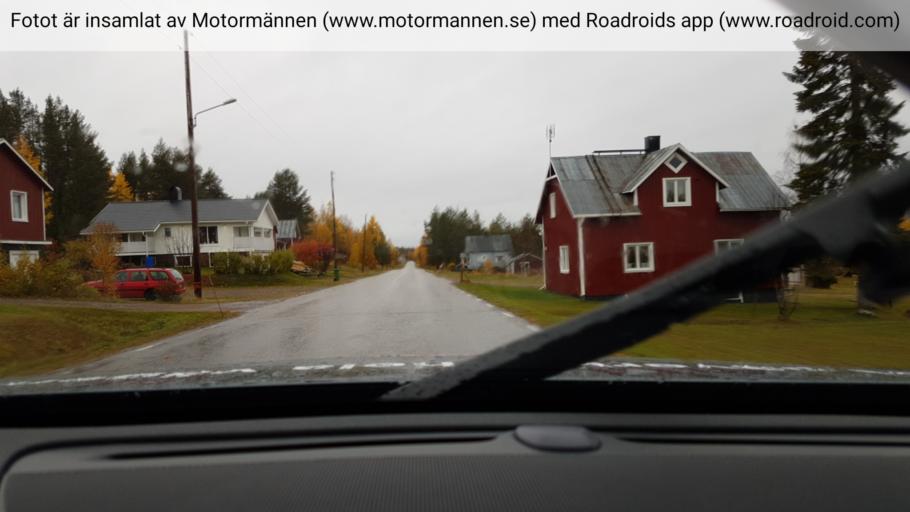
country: SE
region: Norrbotten
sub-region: Pajala Kommun
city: Pajala
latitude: 66.9118
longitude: 23.0217
